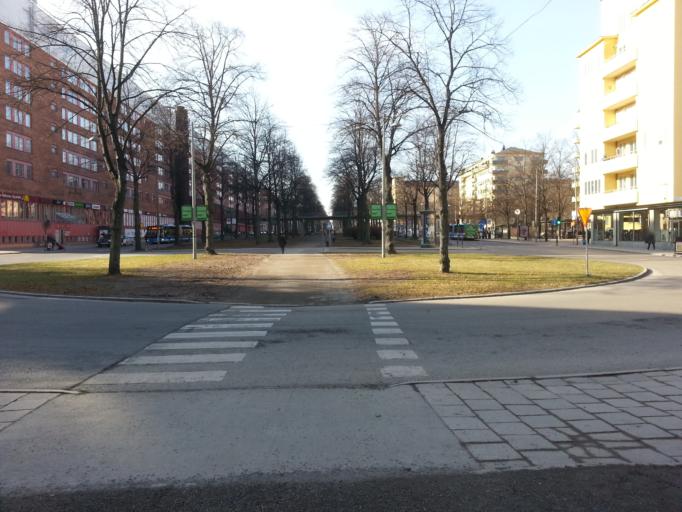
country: SE
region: Stockholm
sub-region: Stockholms Kommun
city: OEstermalm
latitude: 59.3397
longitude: 18.0948
